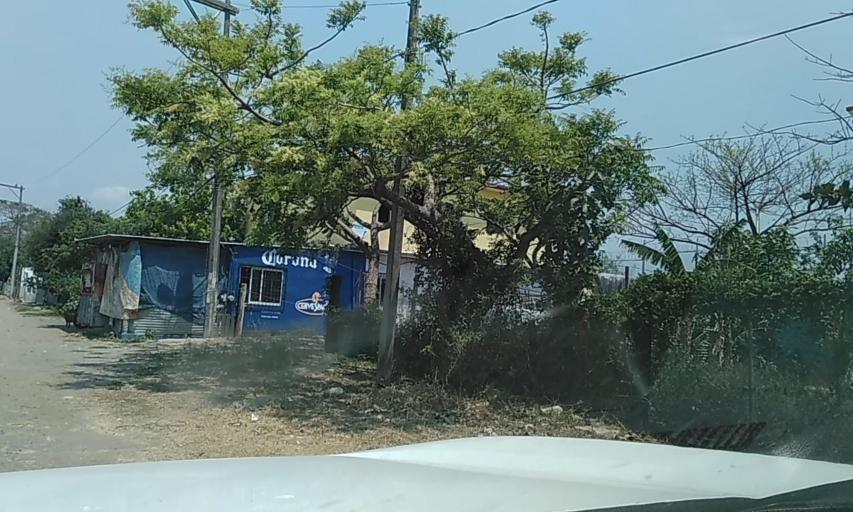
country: MX
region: Veracruz
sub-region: Veracruz
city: Las Amapolas
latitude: 19.1394
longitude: -96.1947
